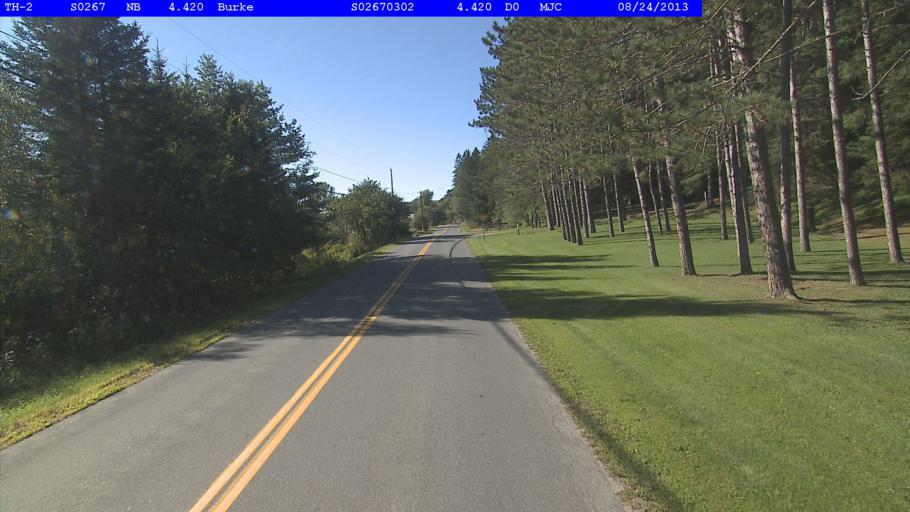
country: US
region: Vermont
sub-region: Caledonia County
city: Lyndonville
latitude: 44.6370
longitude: -71.9725
